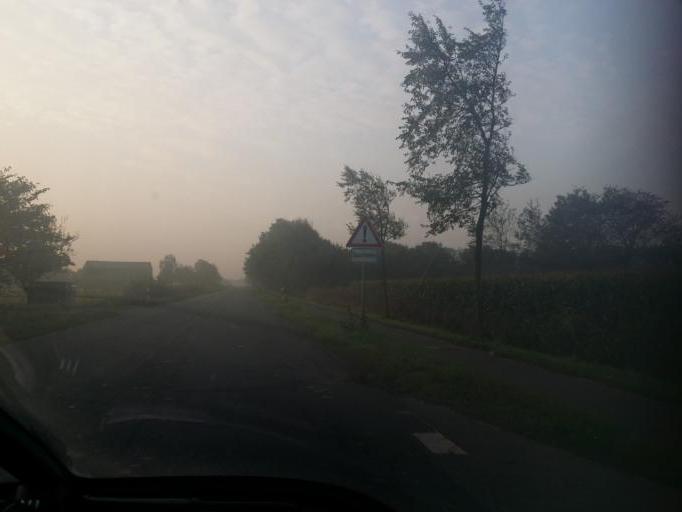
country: DE
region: Schleswig-Holstein
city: Elisabeth-Sophien-Koog
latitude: 54.5106
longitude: 8.9356
